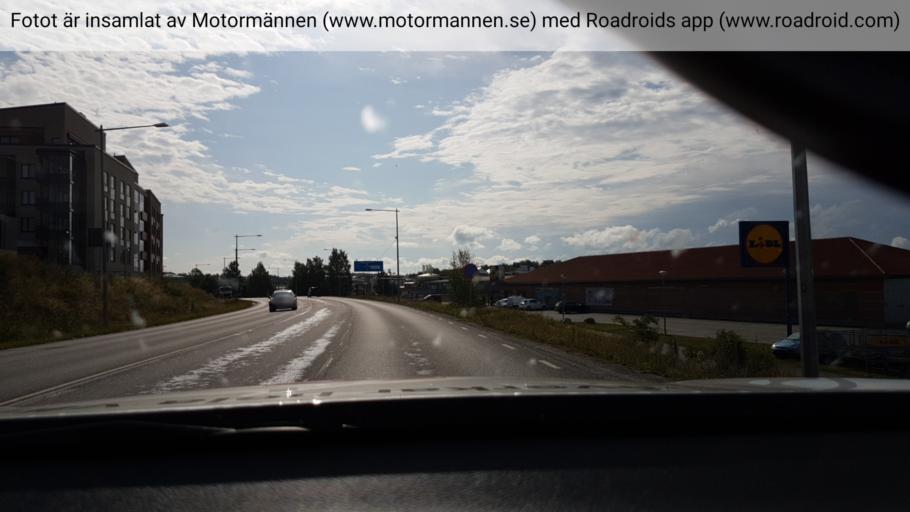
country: SE
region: Stockholm
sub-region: Osterakers Kommun
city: Akersberga
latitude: 59.4809
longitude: 18.2861
